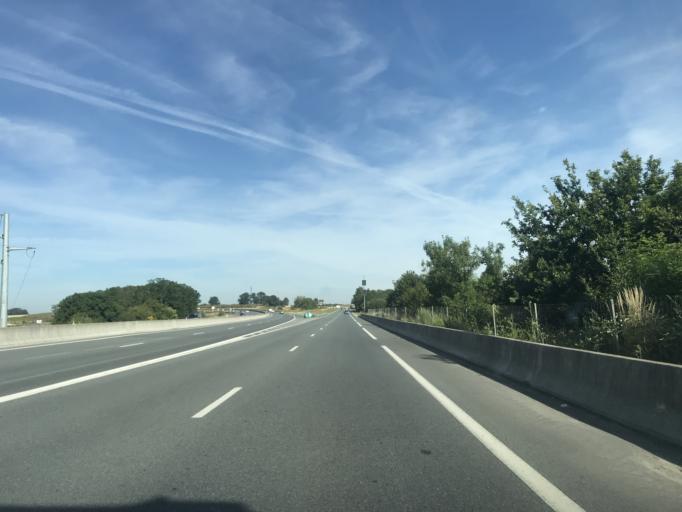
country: FR
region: Haute-Normandie
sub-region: Departement de la Seine-Maritime
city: Roumare
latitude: 49.5215
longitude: 0.9717
